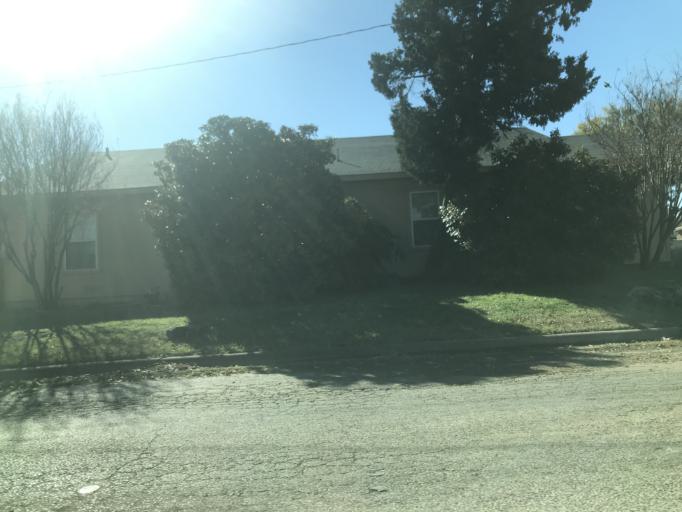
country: US
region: Texas
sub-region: Taylor County
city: Abilene
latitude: 32.4639
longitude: -99.7350
